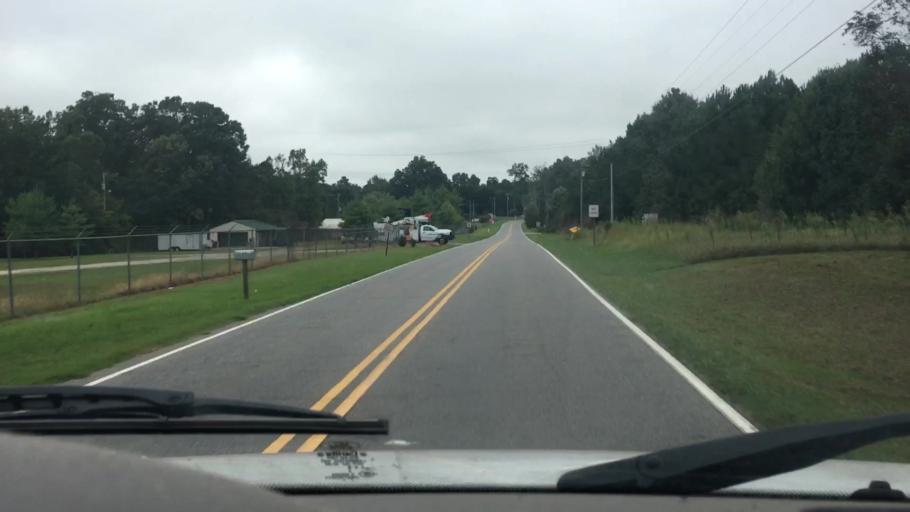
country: US
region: North Carolina
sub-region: Catawba County
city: Lake Norman of Catawba
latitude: 35.5532
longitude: -80.9936
